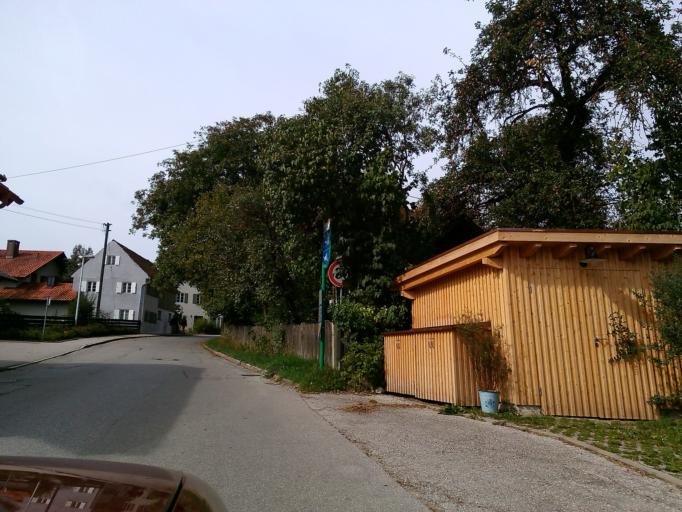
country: DE
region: Bavaria
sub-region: Upper Bavaria
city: Pocking
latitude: 47.9854
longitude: 11.2899
